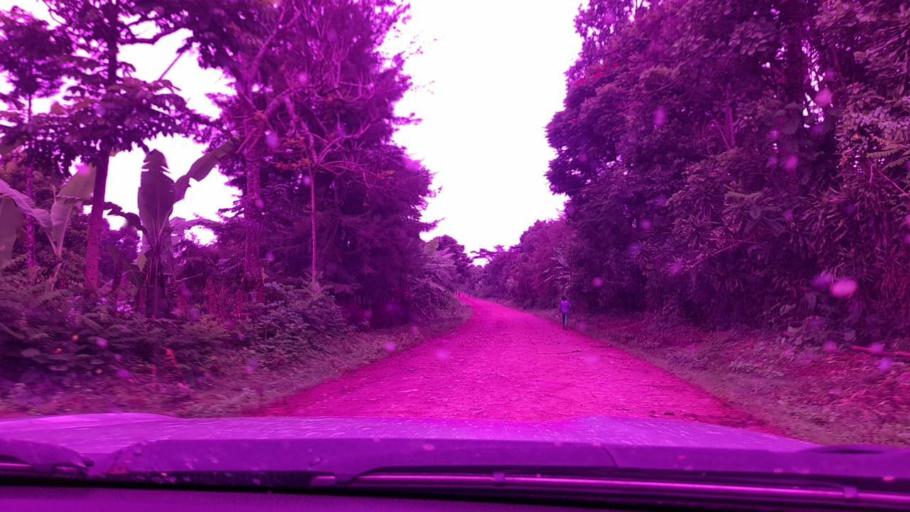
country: ET
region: Southern Nations, Nationalities, and People's Region
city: Bonga
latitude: 7.5507
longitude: 35.8688
